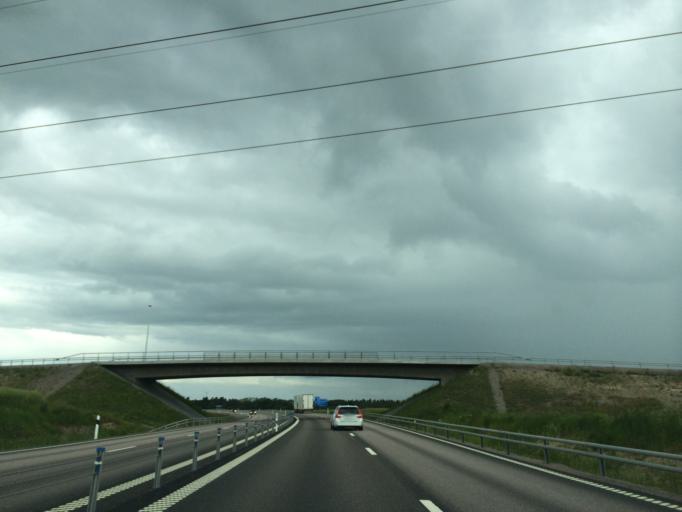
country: SE
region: OEstergoetland
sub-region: Mjolby Kommun
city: Mjolby
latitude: 58.3921
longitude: 15.1059
